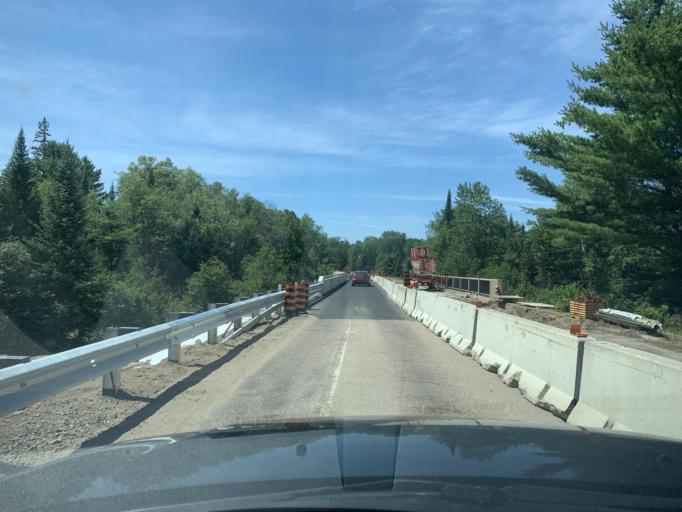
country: CA
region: Ontario
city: Petawawa
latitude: 45.6661
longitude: -77.5738
